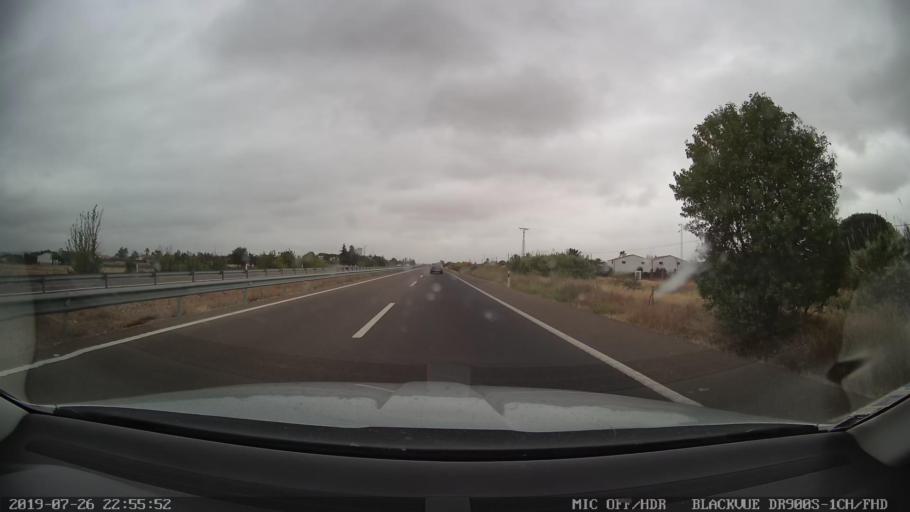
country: ES
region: Extremadura
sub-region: Provincia de Badajoz
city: Calamonte
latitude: 38.8903
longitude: -6.4252
